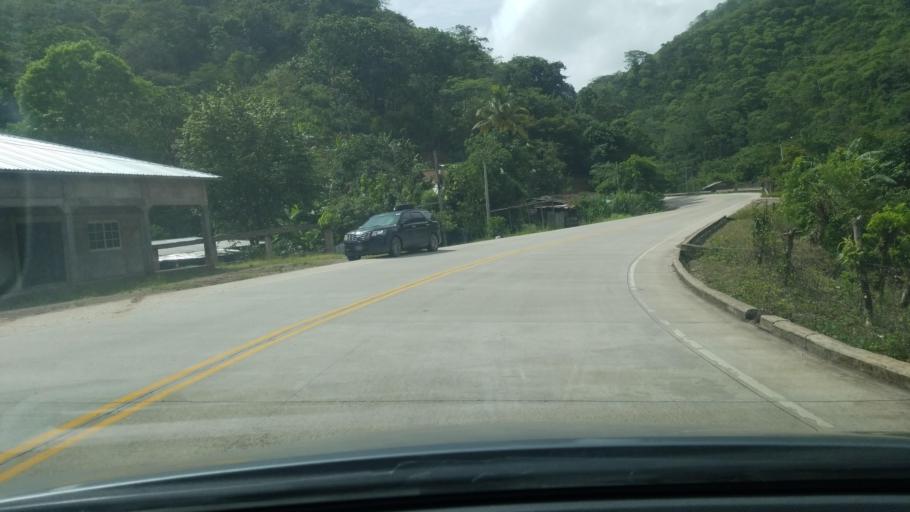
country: HN
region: Copan
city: Buenos Aires
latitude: 14.9321
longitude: -88.9628
